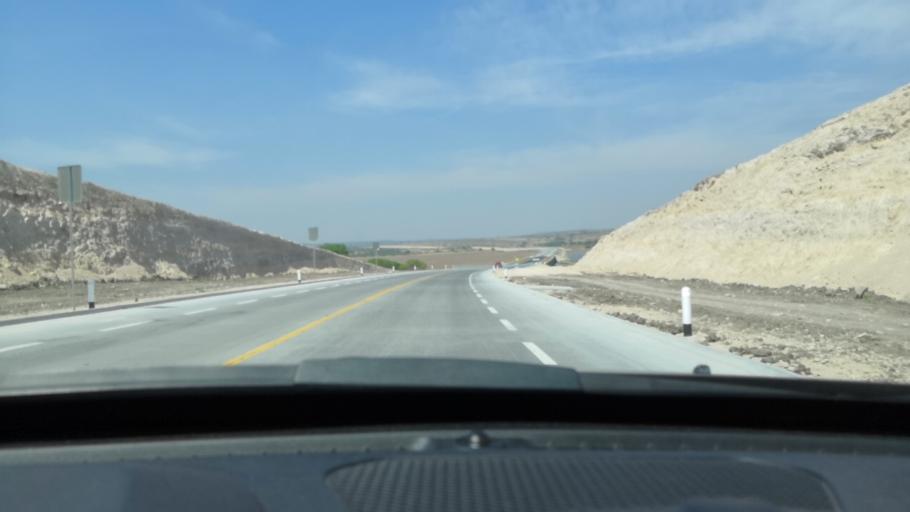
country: MX
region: Guanajuato
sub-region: Purisima del Rincon
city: Potrerillos (Guanajal)
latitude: 21.0834
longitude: -101.8380
